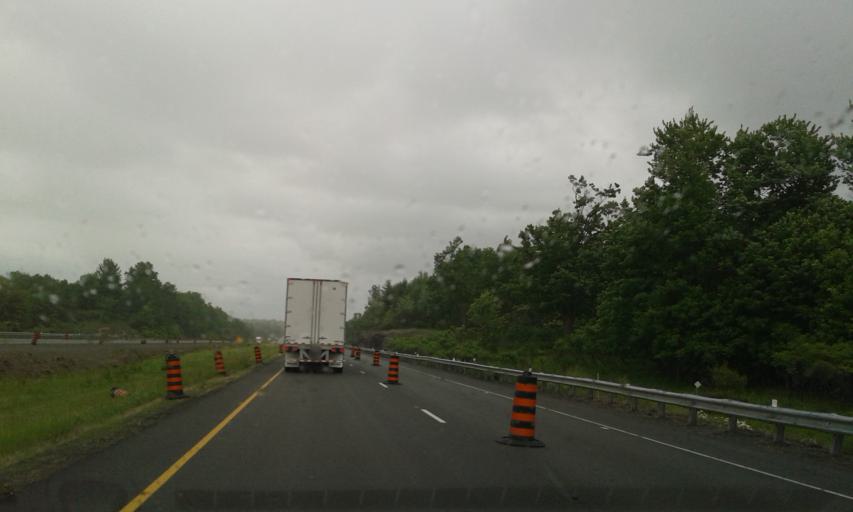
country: CA
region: Ontario
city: Gananoque
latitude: 44.3694
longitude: -76.0594
